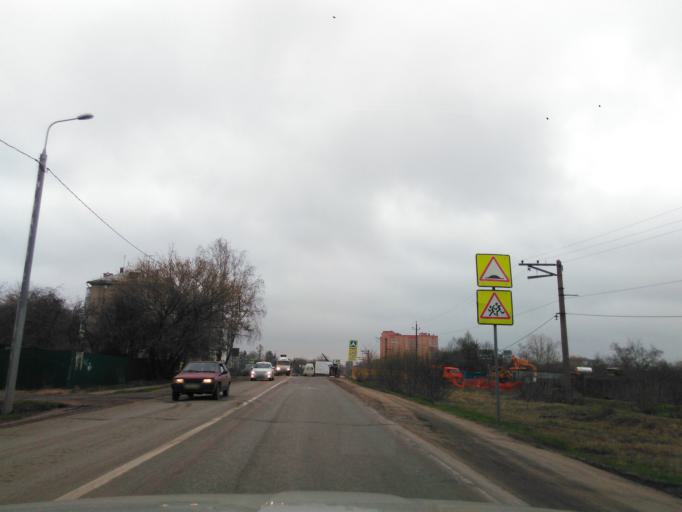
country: RU
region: Moskovskaya
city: Nakhabino
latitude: 55.8356
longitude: 37.1562
